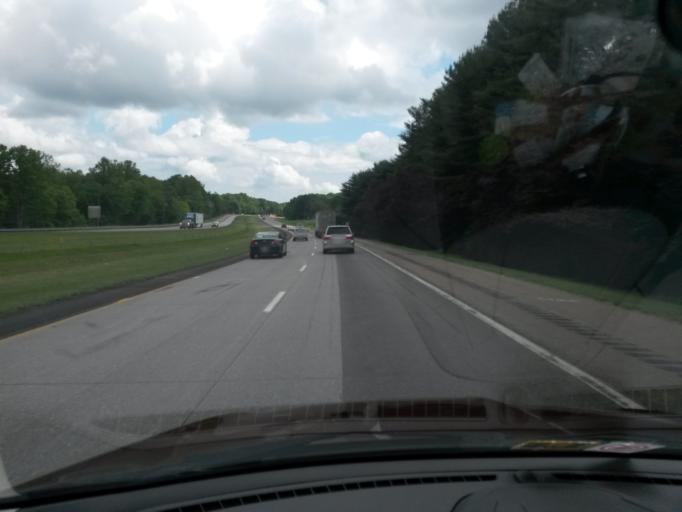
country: US
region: Virginia
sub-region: Carroll County
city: Cana
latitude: 36.5611
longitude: -80.7447
